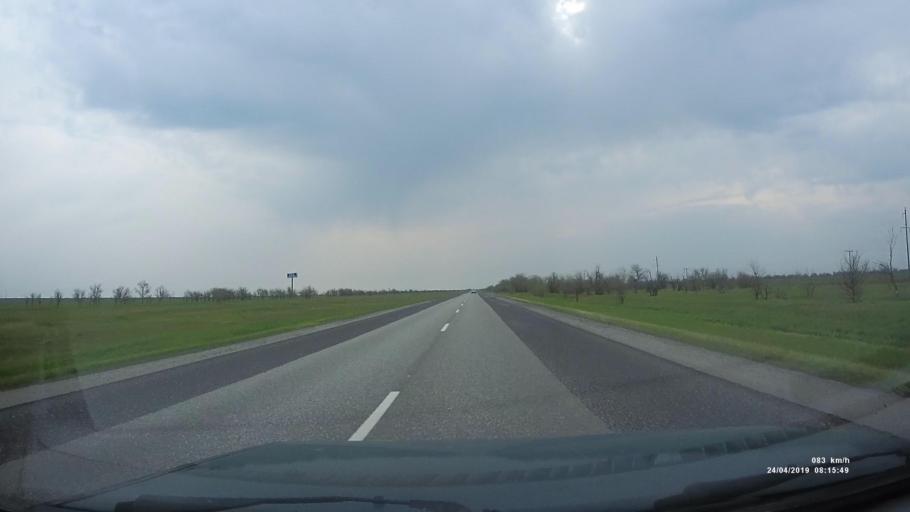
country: RU
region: Kalmykiya
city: Priyutnoye
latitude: 46.0996
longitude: 43.6013
